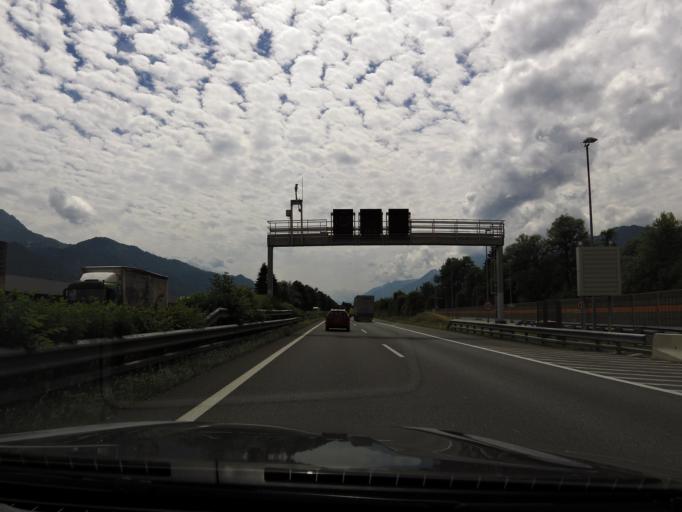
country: AT
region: Tyrol
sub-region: Politischer Bezirk Kufstein
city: Breitenbach am Inn
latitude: 47.4746
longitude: 11.9734
